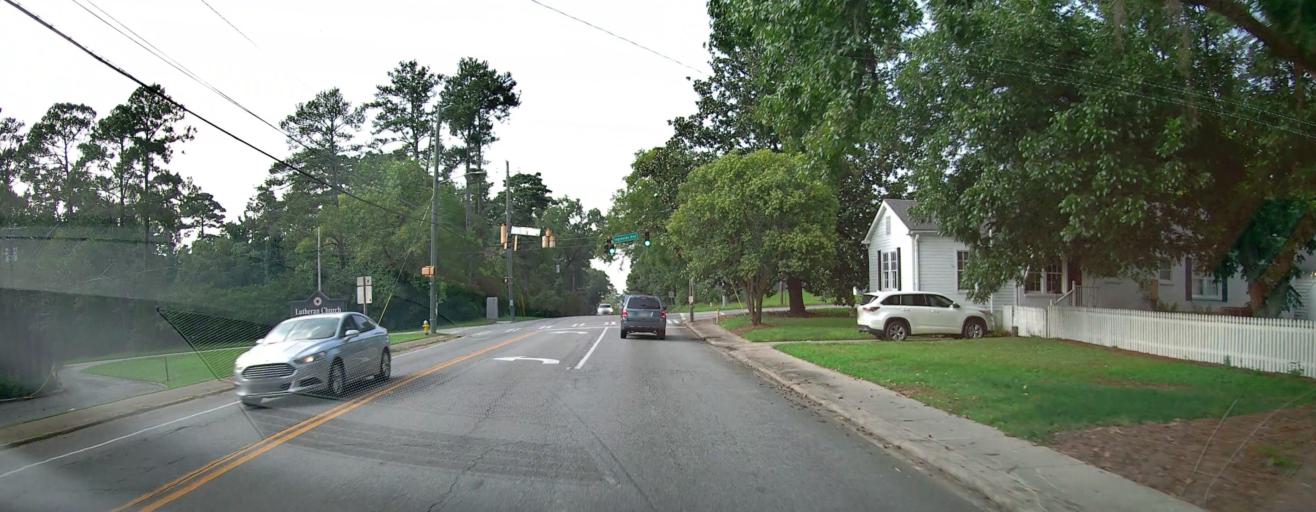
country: US
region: Georgia
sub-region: Bibb County
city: Macon
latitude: 32.8533
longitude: -83.6624
